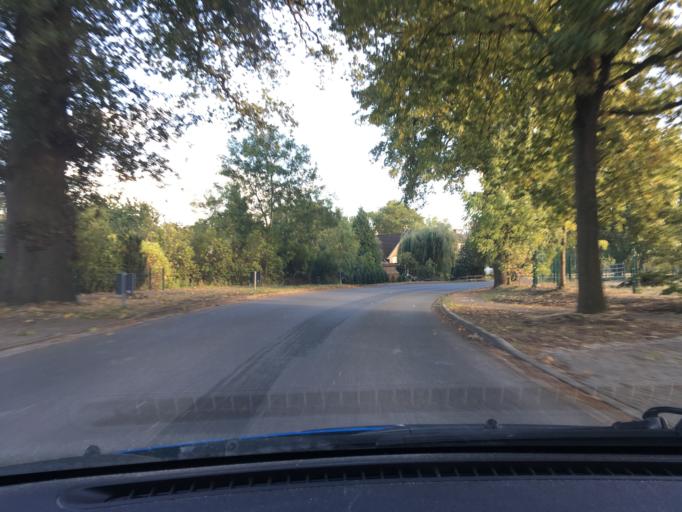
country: DE
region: Lower Saxony
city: Hittbergen
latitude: 53.3261
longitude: 10.5972
